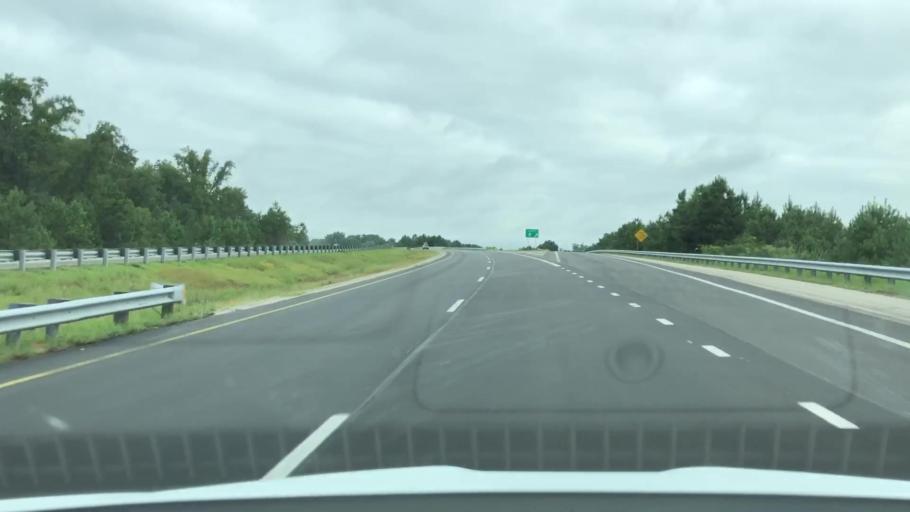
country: US
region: North Carolina
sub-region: Wilson County
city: Lucama
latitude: 35.6643
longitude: -77.9556
